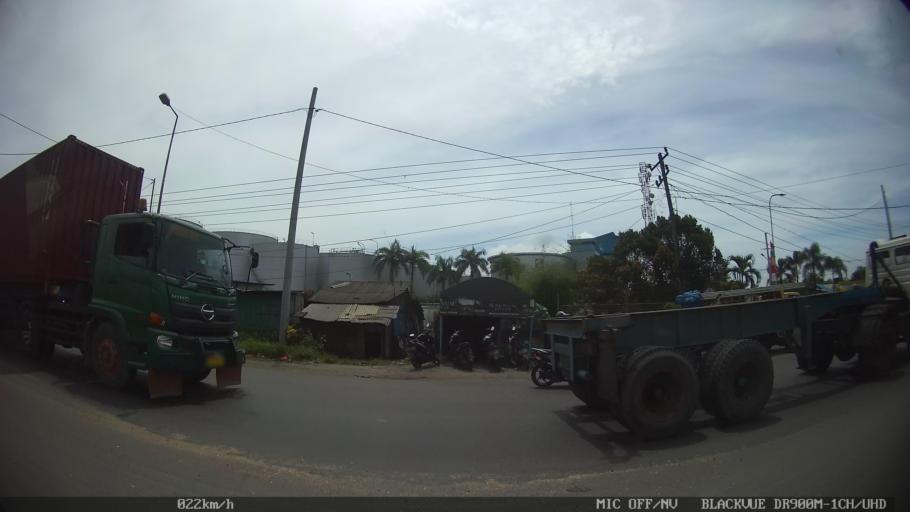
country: ID
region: North Sumatra
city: Belawan
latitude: 3.7787
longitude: 98.6873
